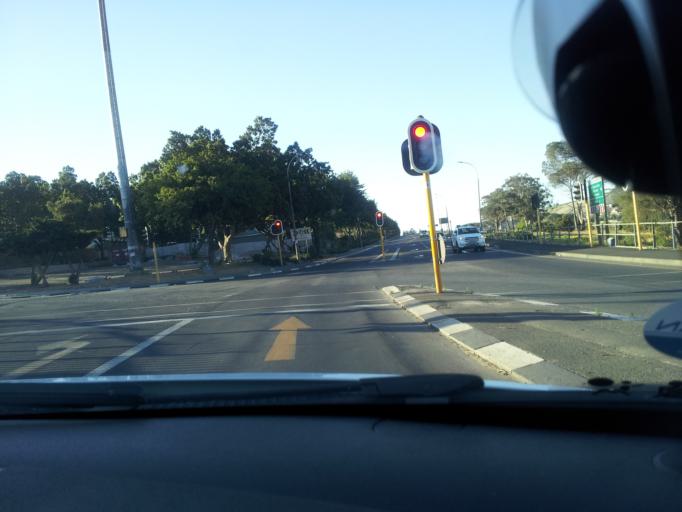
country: ZA
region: Western Cape
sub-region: Cape Winelands District Municipality
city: Stellenbosch
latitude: -33.9190
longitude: 18.8523
